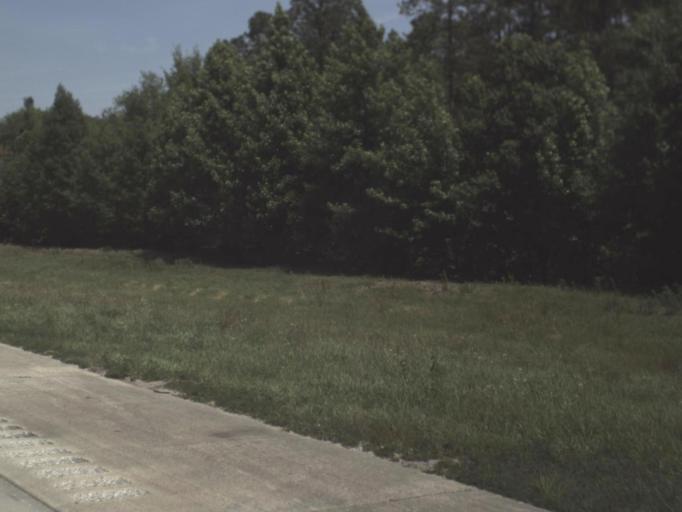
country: US
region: Florida
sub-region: Saint Johns County
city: Palm Valley
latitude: 30.2011
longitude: -81.5136
